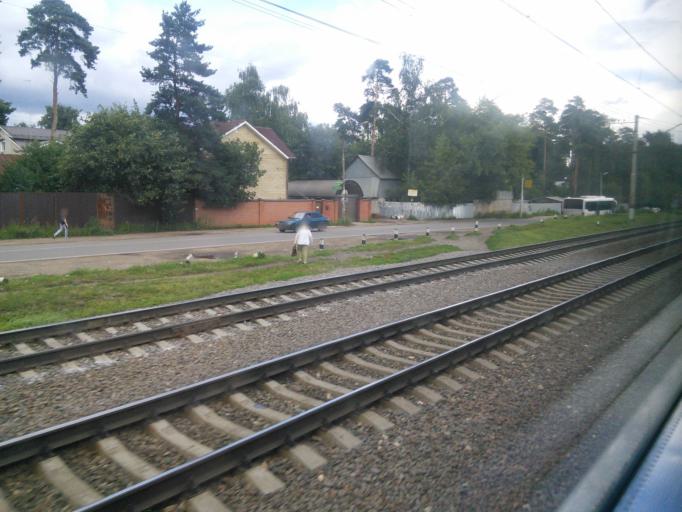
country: RU
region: Moskovskaya
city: Malakhovka
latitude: 55.6444
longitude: 38.0128
